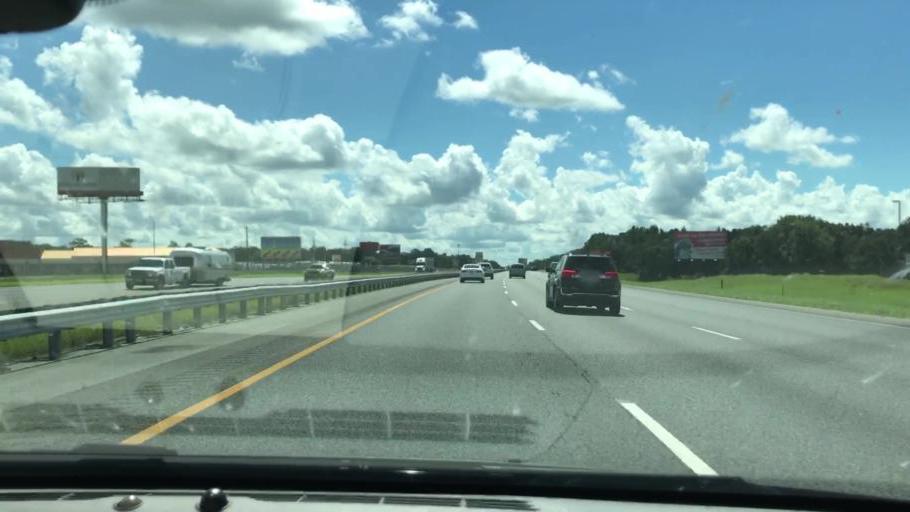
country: US
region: Georgia
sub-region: Lowndes County
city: Valdosta
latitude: 30.6765
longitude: -83.2193
